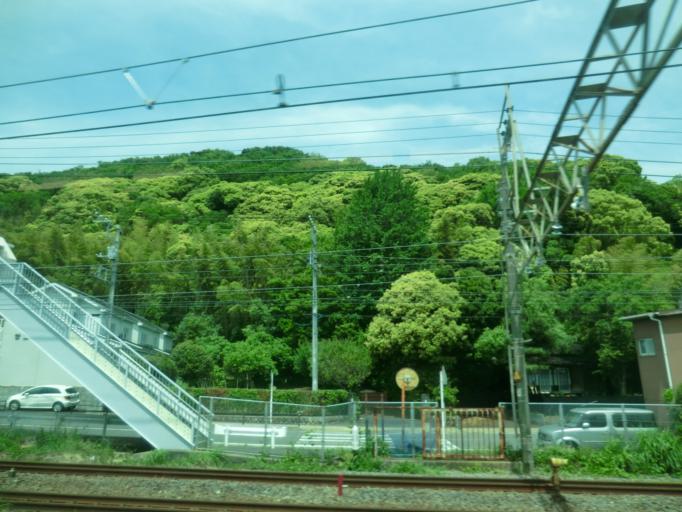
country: JP
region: Kanagawa
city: Ninomiya
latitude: 35.2974
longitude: 139.2538
